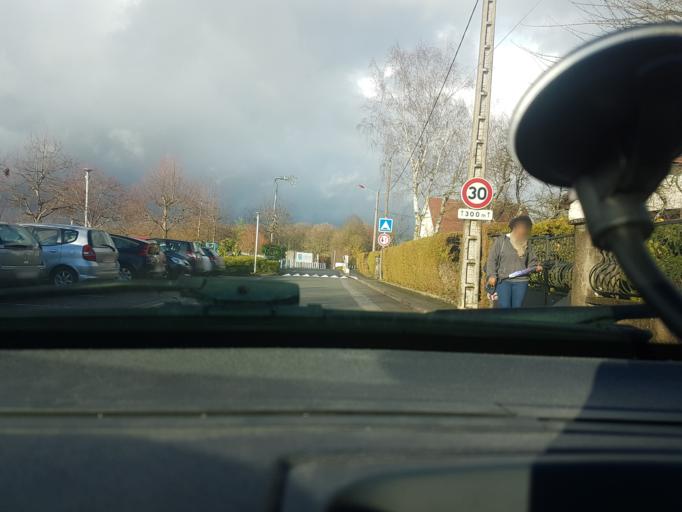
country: FR
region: Franche-Comte
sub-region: Territoire de Belfort
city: Andelnans
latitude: 47.5875
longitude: 6.8671
